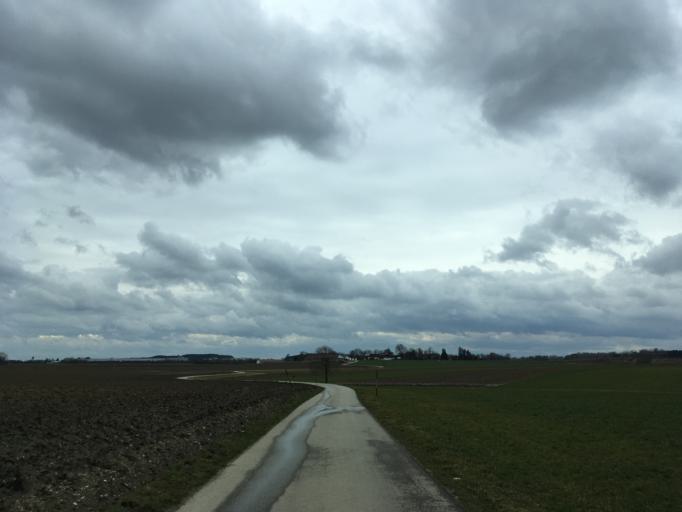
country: DE
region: Bavaria
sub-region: Upper Bavaria
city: Markt Schwaben
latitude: 48.1759
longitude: 11.8571
